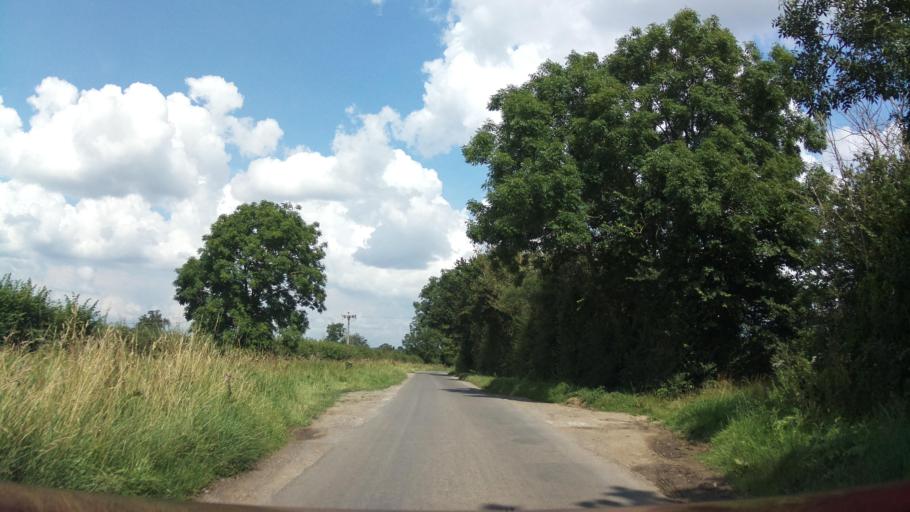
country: GB
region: England
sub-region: Wiltshire
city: Hankerton
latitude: 51.5959
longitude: -2.0344
